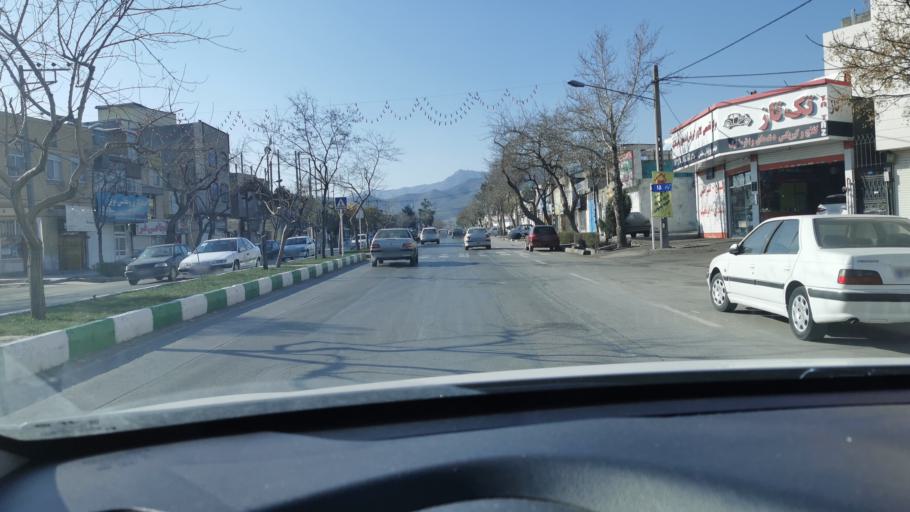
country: IR
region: Razavi Khorasan
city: Mashhad
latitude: 36.2744
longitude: 59.5761
